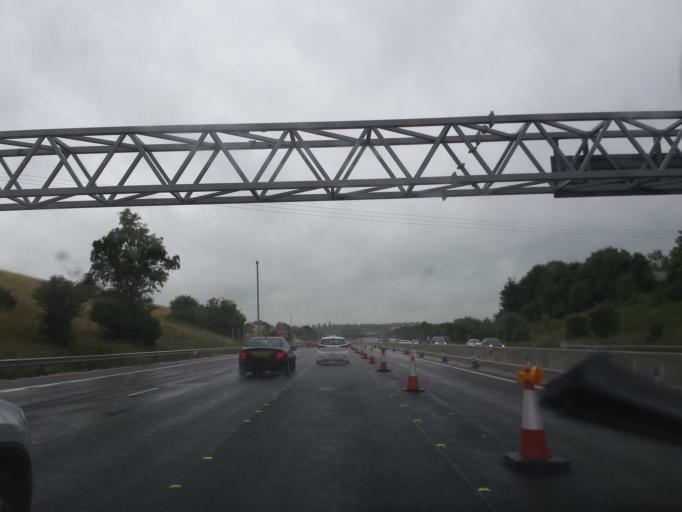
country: GB
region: England
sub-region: Rotherham
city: Wales
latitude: 53.3562
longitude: -1.2849
